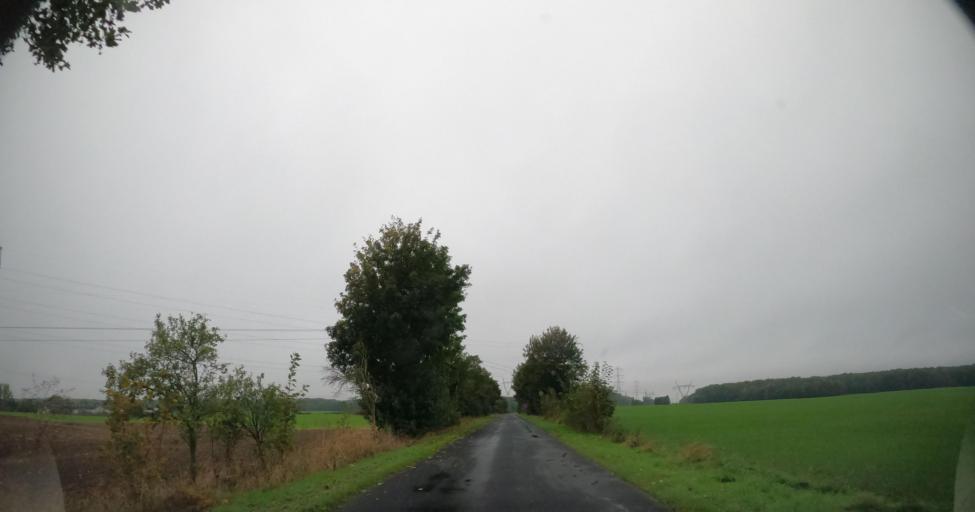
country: PL
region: West Pomeranian Voivodeship
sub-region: Powiat pyrzycki
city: Kozielice
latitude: 53.0503
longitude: 14.7523
